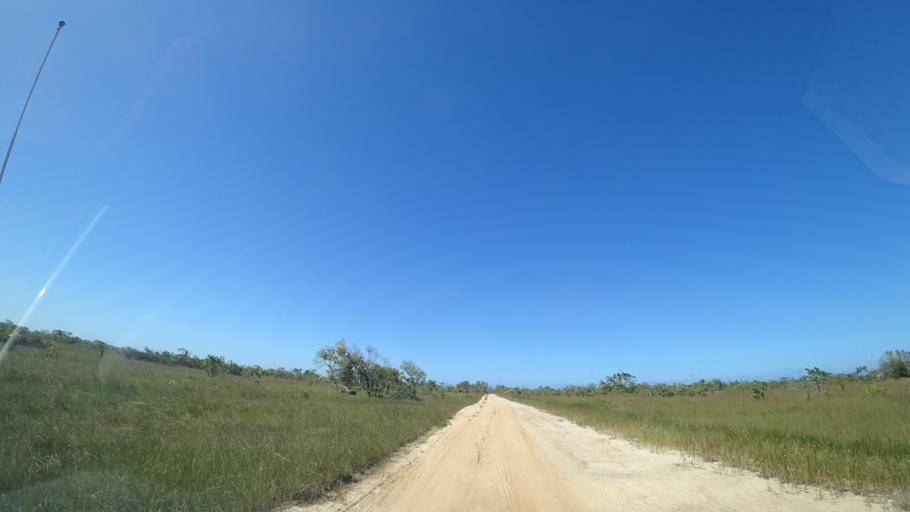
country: MZ
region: Sofala
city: Beira
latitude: -19.5731
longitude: 35.2290
